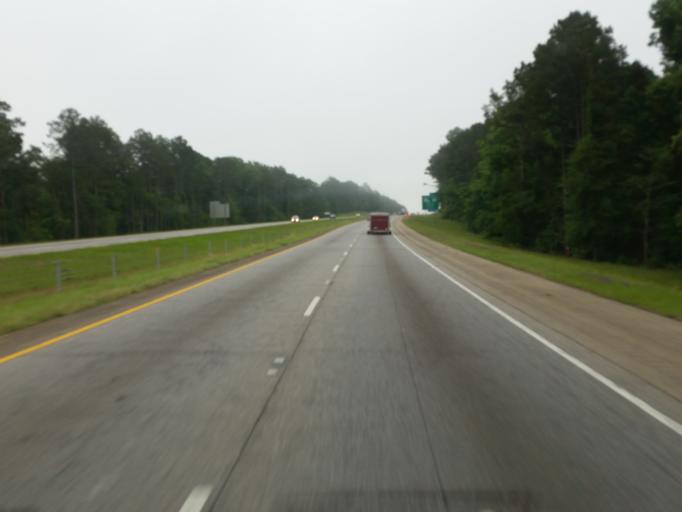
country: US
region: Louisiana
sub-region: Webster Parish
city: Minden
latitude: 32.5937
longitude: -93.3106
